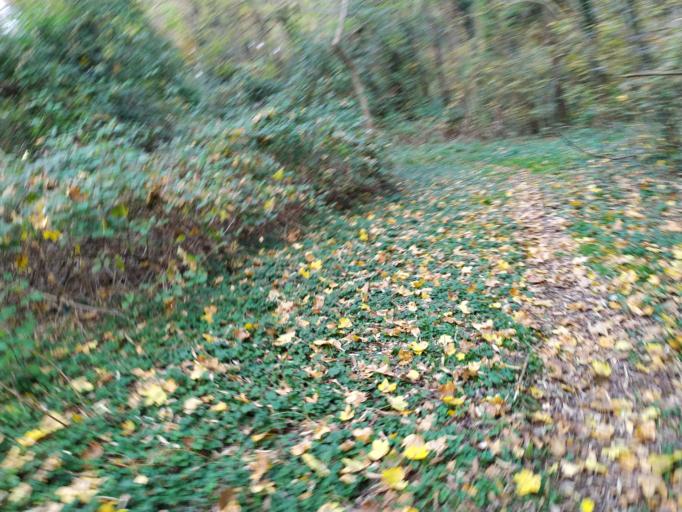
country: IT
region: Veneto
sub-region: Provincia di Vicenza
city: Monte di Malo
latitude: 45.6859
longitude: 11.3604
